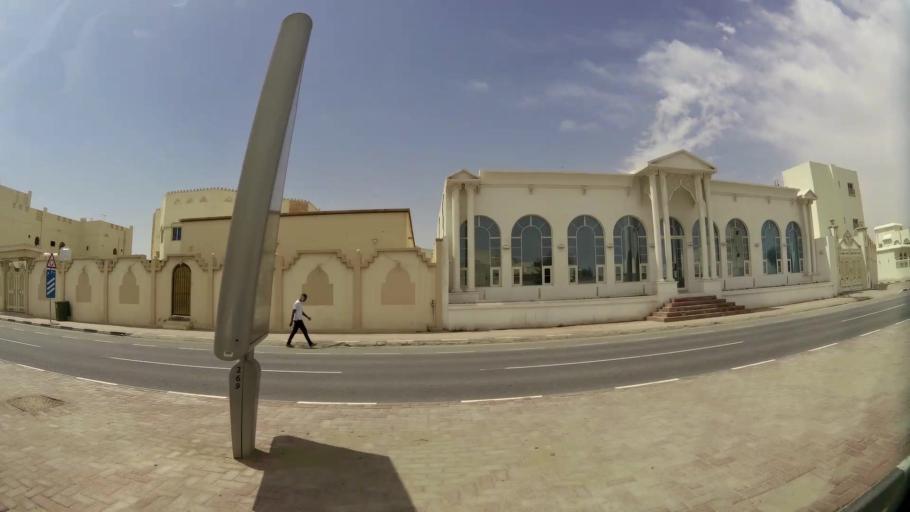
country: QA
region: Baladiyat ar Rayyan
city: Ar Rayyan
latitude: 25.2878
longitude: 51.4174
